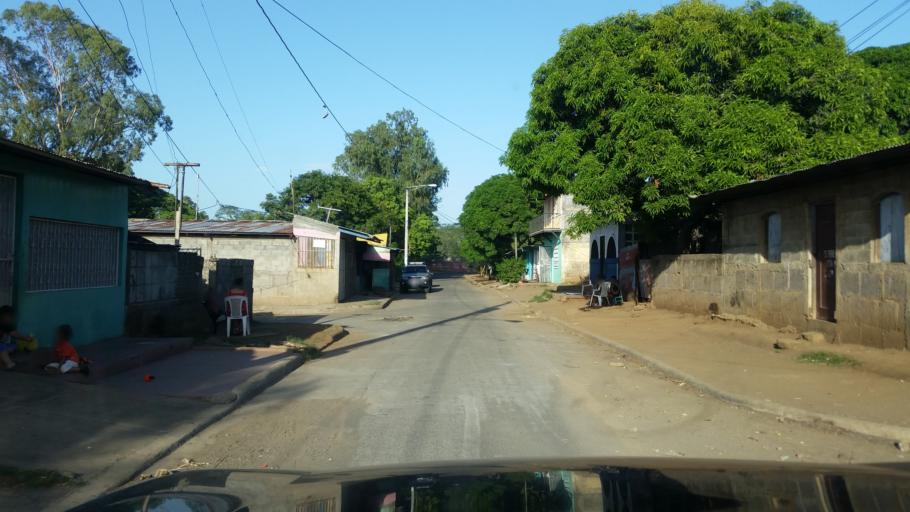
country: NI
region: Managua
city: Managua
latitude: 12.1269
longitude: -86.2853
